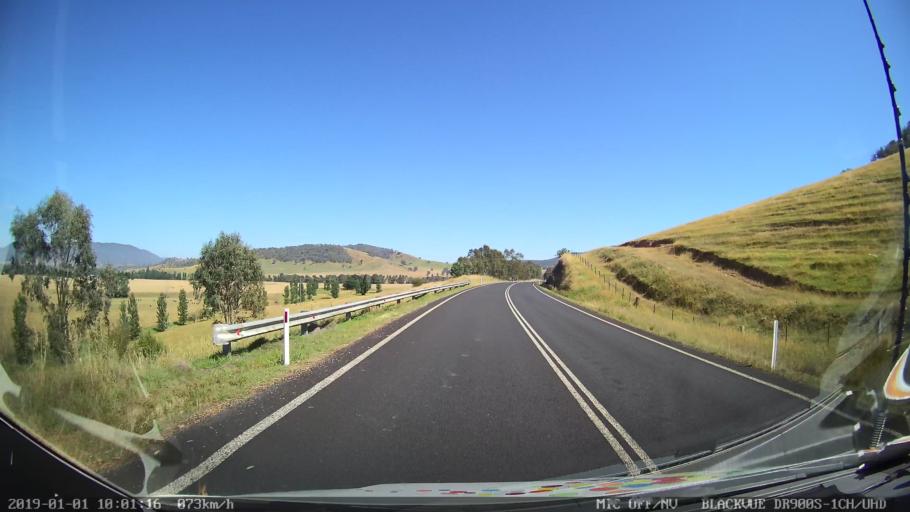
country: AU
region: New South Wales
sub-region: Snowy River
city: Jindabyne
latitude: -36.1933
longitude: 148.1021
